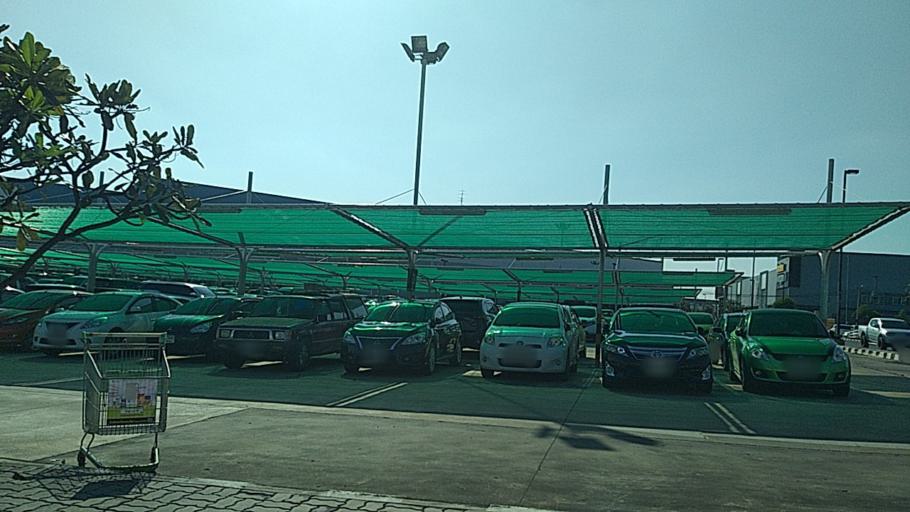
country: TH
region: Phra Nakhon Si Ayutthaya
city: Ban Bang Kadi Pathum Thani
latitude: 13.9914
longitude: 100.6203
